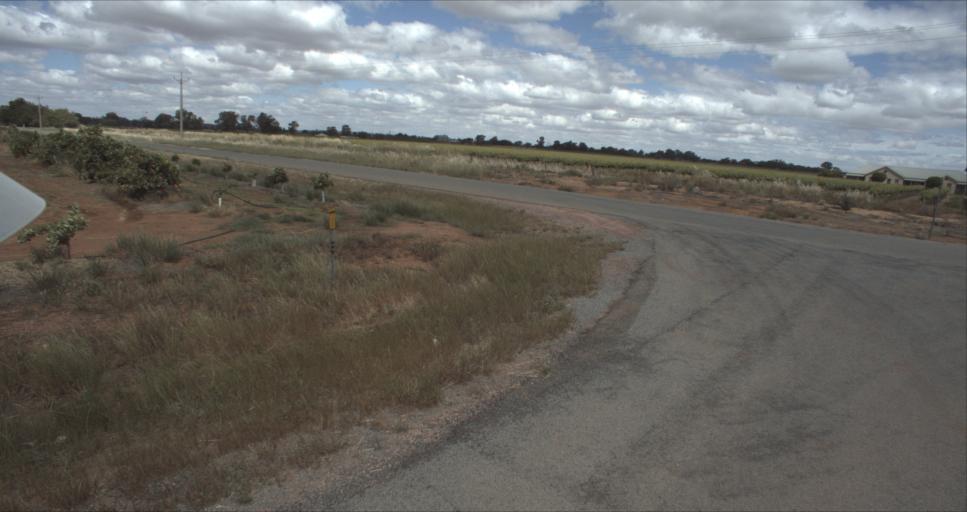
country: AU
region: New South Wales
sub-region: Leeton
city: Leeton
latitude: -34.5889
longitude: 146.3908
